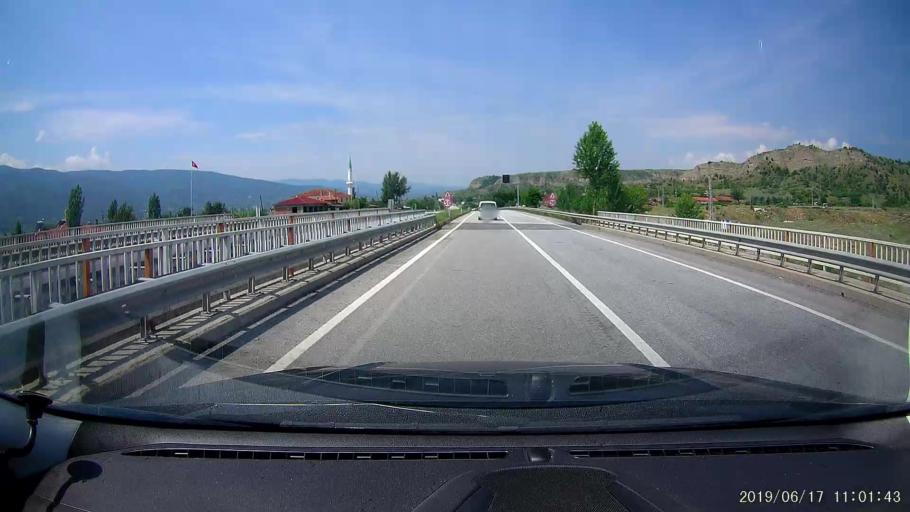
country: TR
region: Kastamonu
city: Tosya
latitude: 41.0249
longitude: 34.1498
